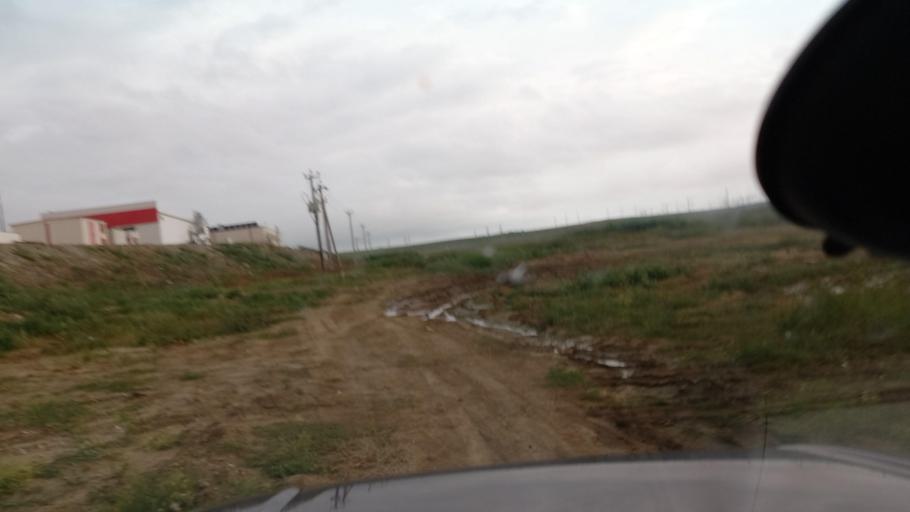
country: RU
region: Krasnodarskiy
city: Taman'
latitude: 45.2112
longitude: 36.7585
